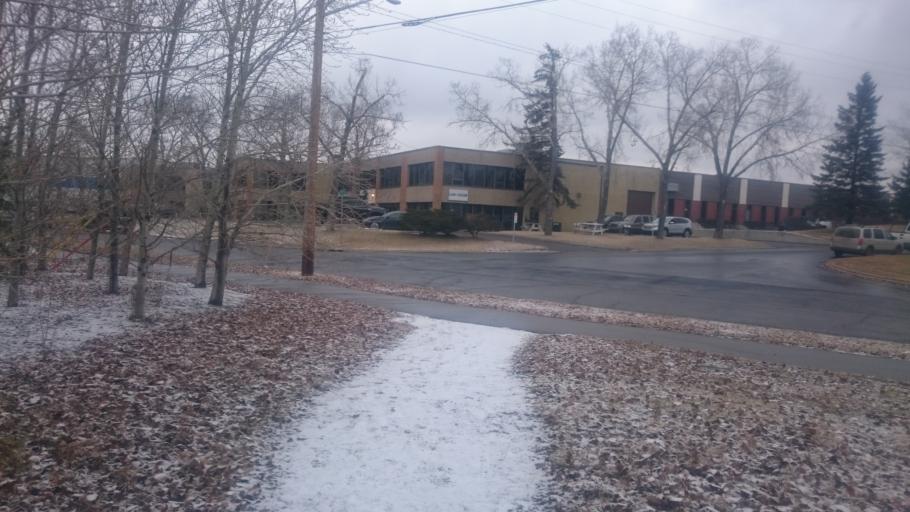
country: CA
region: Alberta
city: Calgary
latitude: 51.0850
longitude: -114.0352
